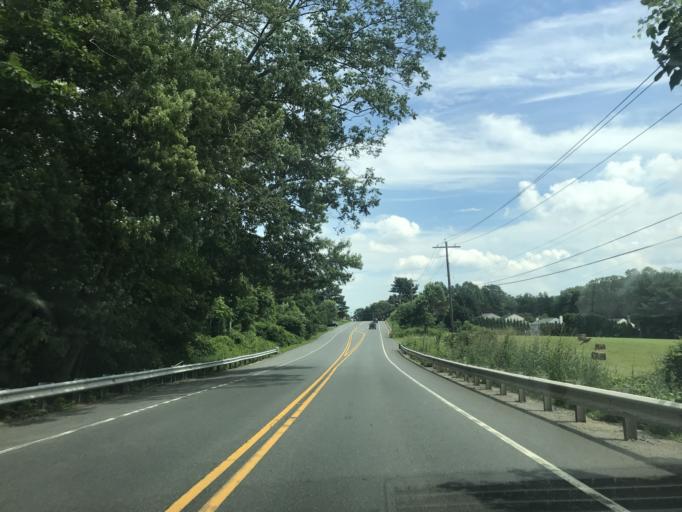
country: US
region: Delaware
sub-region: New Castle County
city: Hockessin
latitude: 39.7680
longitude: -75.6576
